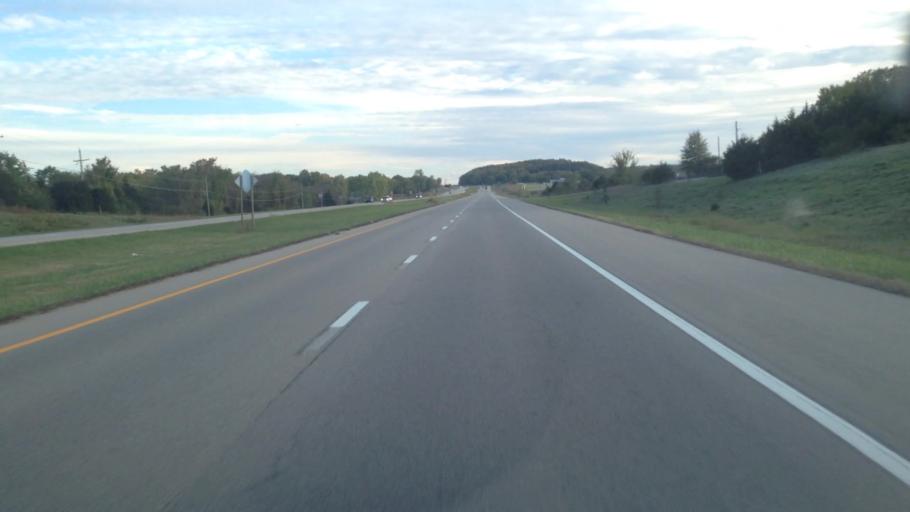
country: US
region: Kansas
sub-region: Douglas County
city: Lawrence
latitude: 38.9058
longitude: -95.2608
